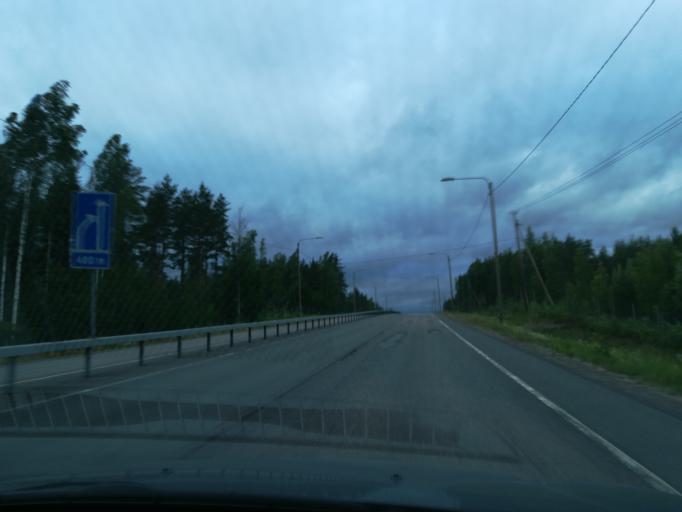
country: FI
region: Southern Savonia
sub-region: Mikkeli
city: Ristiina
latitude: 61.4072
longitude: 27.3490
